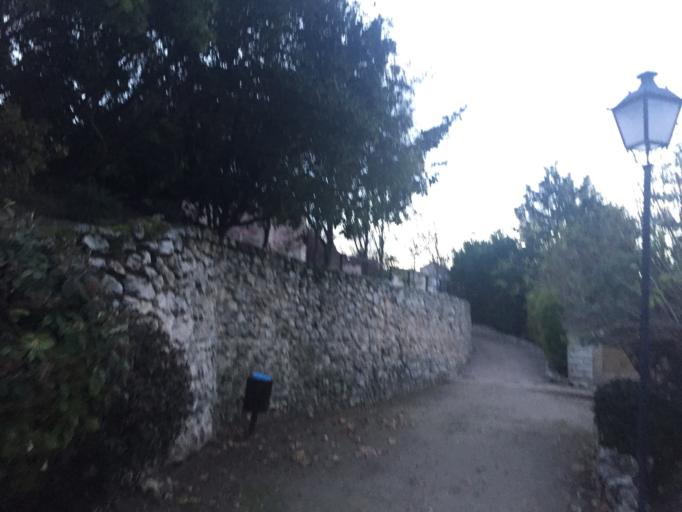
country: ES
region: Castille and Leon
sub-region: Provincia de Valladolid
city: Olmedo
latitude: 41.2902
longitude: -4.6824
